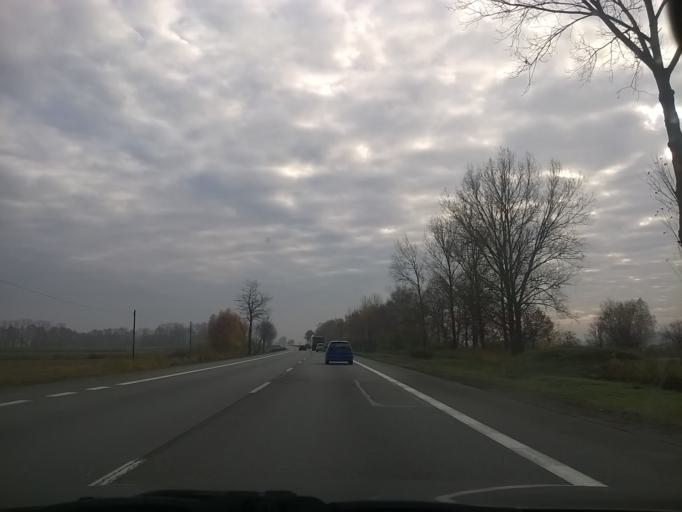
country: PL
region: Pomeranian Voivodeship
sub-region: Powiat gdanski
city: Cedry Wielkie
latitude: 54.2720
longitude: 18.8793
